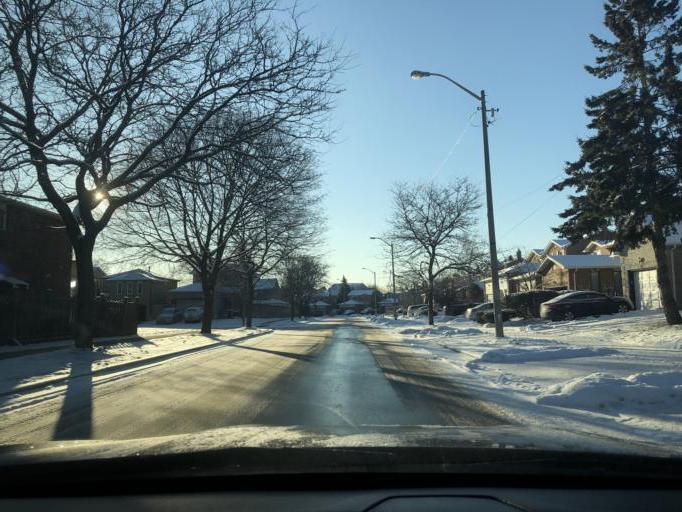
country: CA
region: Ontario
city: Pickering
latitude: 43.7833
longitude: -79.1373
